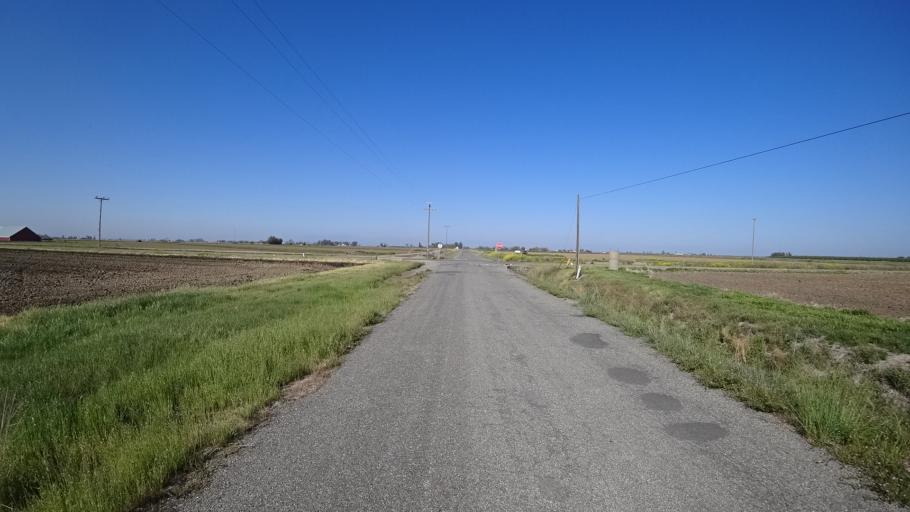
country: US
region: California
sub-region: Glenn County
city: Hamilton City
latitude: 39.6016
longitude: -122.0363
